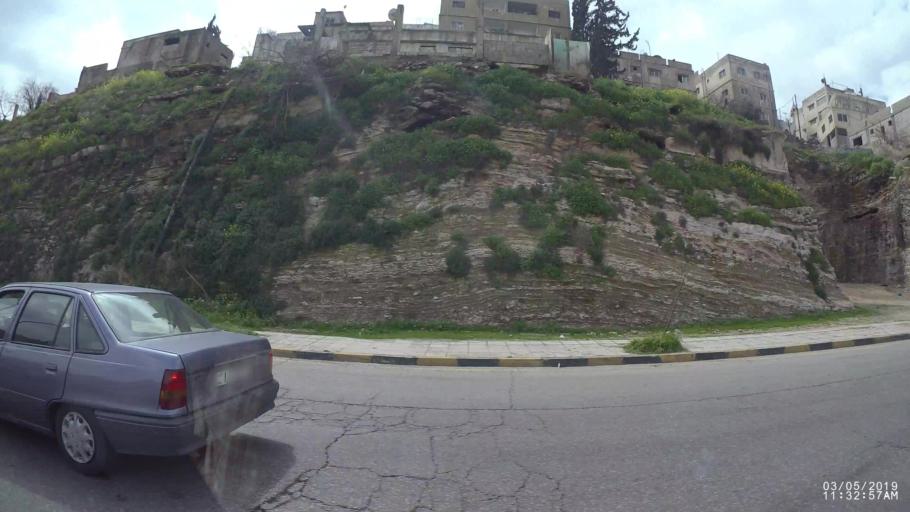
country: JO
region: Amman
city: Amman
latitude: 31.9636
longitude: 35.9554
